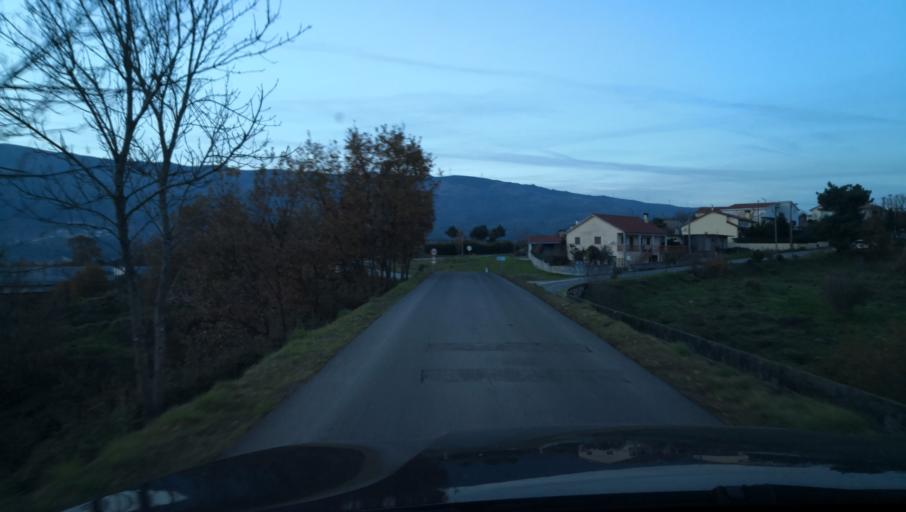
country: PT
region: Vila Real
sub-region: Vila Real
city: Vila Real
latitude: 41.3504
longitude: -7.6991
